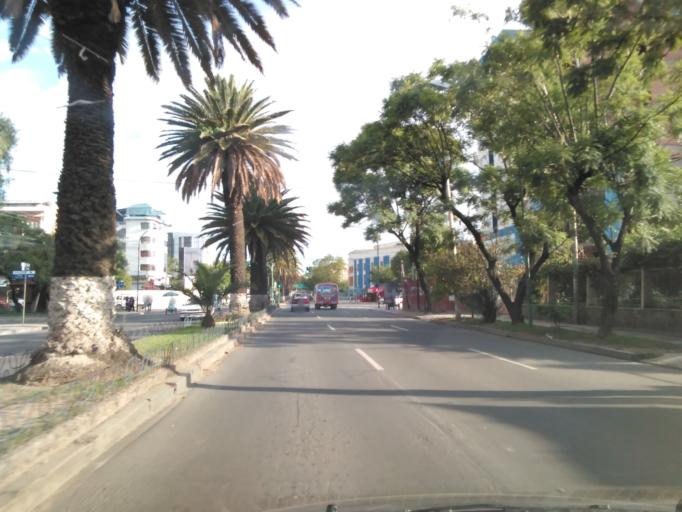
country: BO
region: Cochabamba
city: Cochabamba
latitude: -17.3773
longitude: -66.1613
